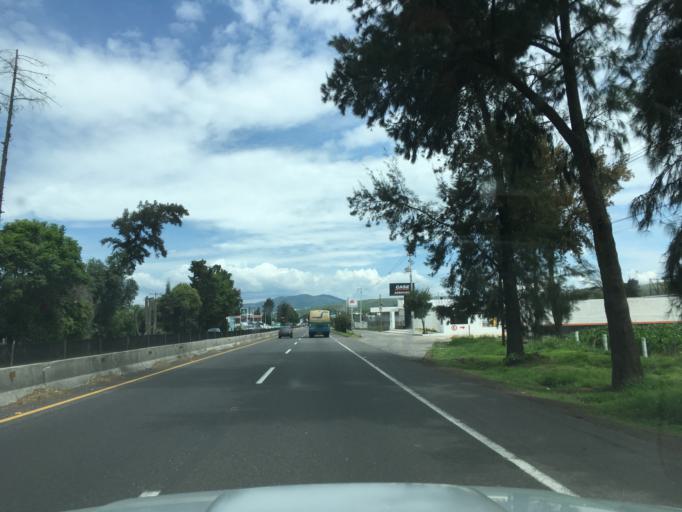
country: MX
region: Michoacan
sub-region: Tarimbaro
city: San Pedro de los Sauces
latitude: 19.7911
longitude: -101.1606
